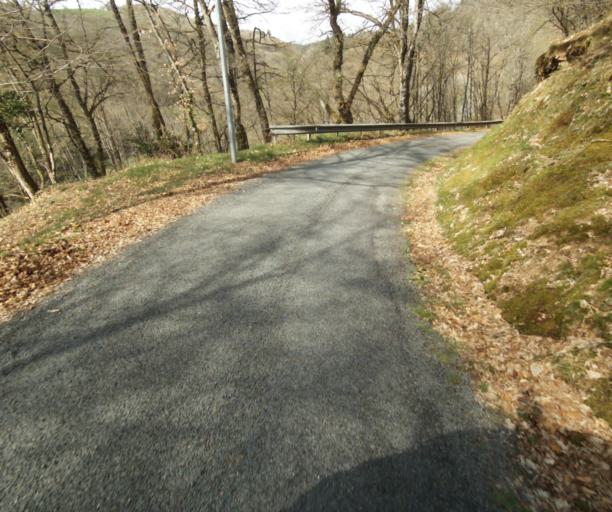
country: FR
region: Limousin
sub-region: Departement de la Correze
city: Naves
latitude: 45.3403
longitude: 1.7915
